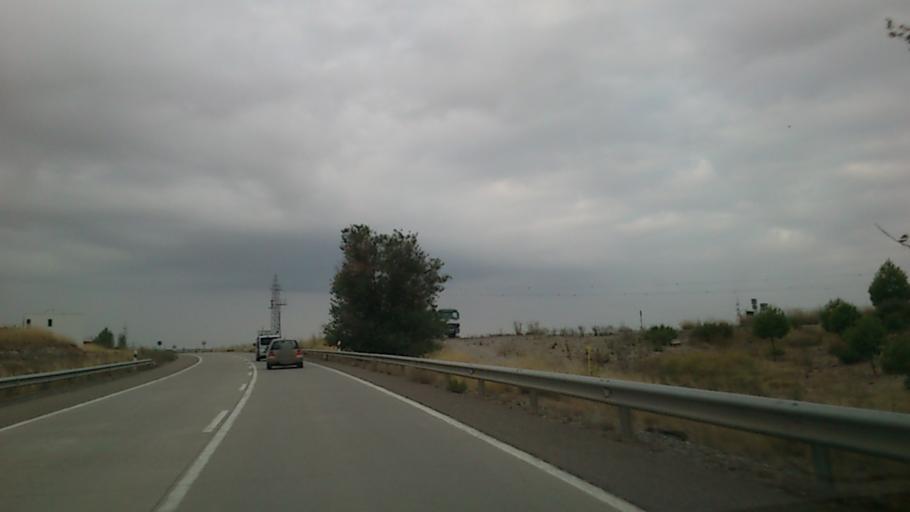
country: ES
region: Aragon
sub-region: Provincia de Zaragoza
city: Villanueva de Gallego
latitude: 41.7798
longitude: -0.8228
